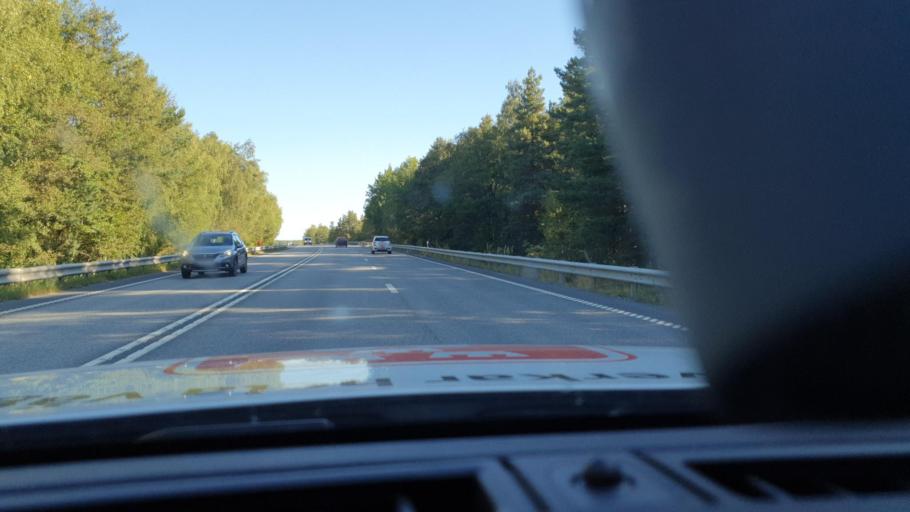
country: SE
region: Stockholm
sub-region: Osterakers Kommun
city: Akersberga
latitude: 59.4376
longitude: 18.2207
